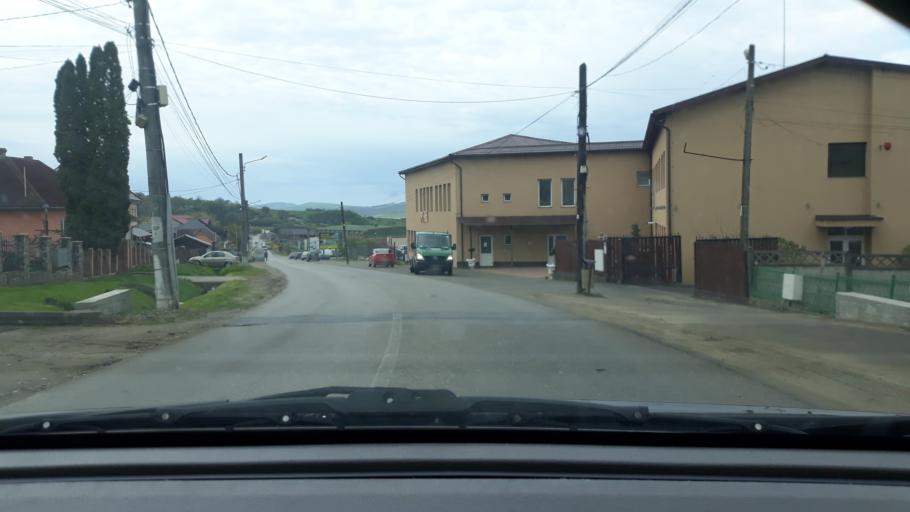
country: RO
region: Salaj
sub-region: Comuna Cehu Silvaniei
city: Cehu Silvaniei
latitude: 47.4078
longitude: 23.1642
